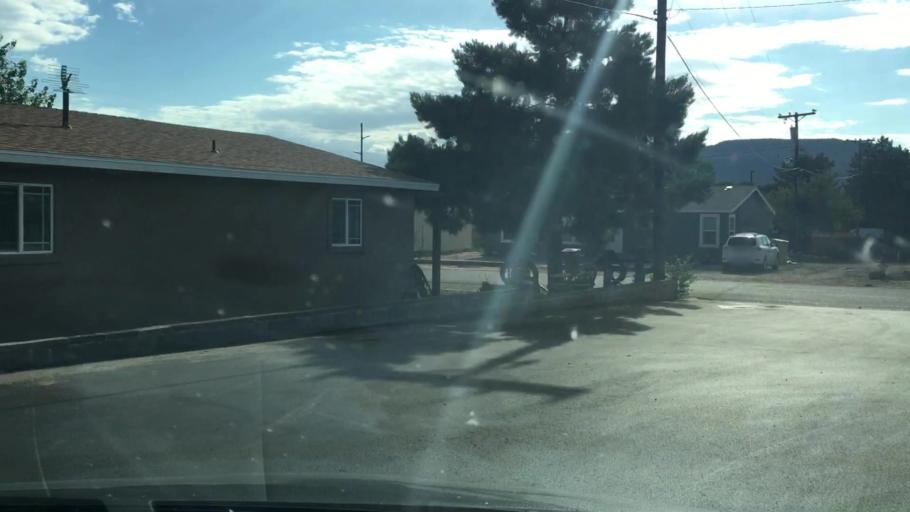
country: US
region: Utah
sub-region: Kane County
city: Kanab
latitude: 37.0421
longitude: -112.5230
